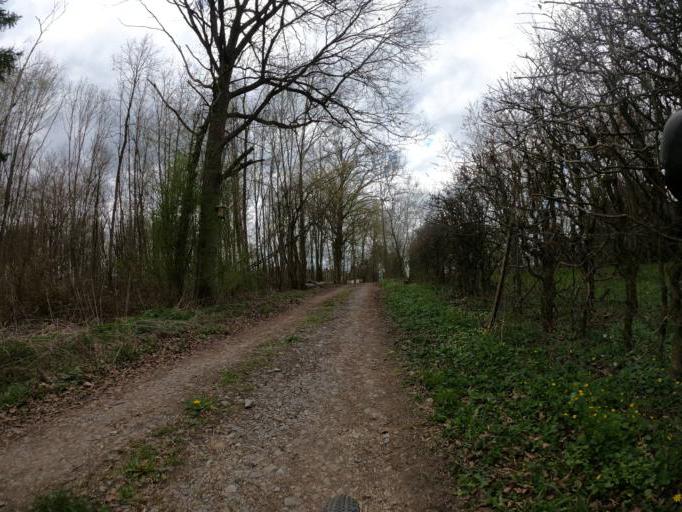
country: DE
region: Baden-Wuerttemberg
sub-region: Tuebingen Region
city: Wannweil
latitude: 48.4850
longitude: 9.1669
